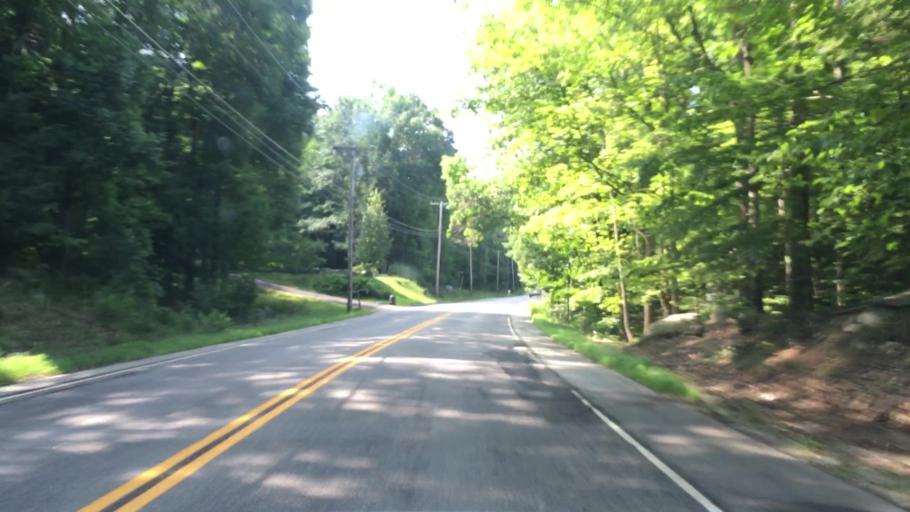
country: US
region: Maine
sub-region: Cumberland County
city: Raymond
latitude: 43.9090
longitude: -70.4405
